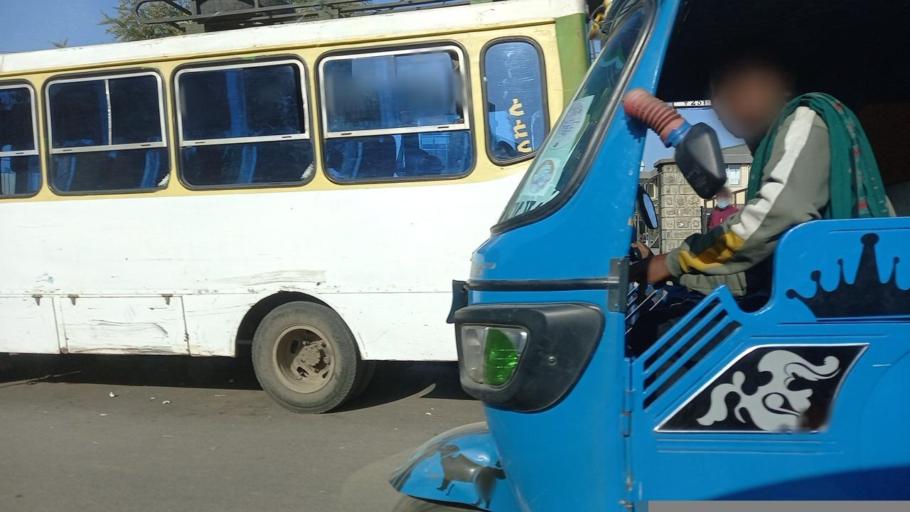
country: ET
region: Adis Abeba
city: Addis Ababa
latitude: 8.9307
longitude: 38.7427
